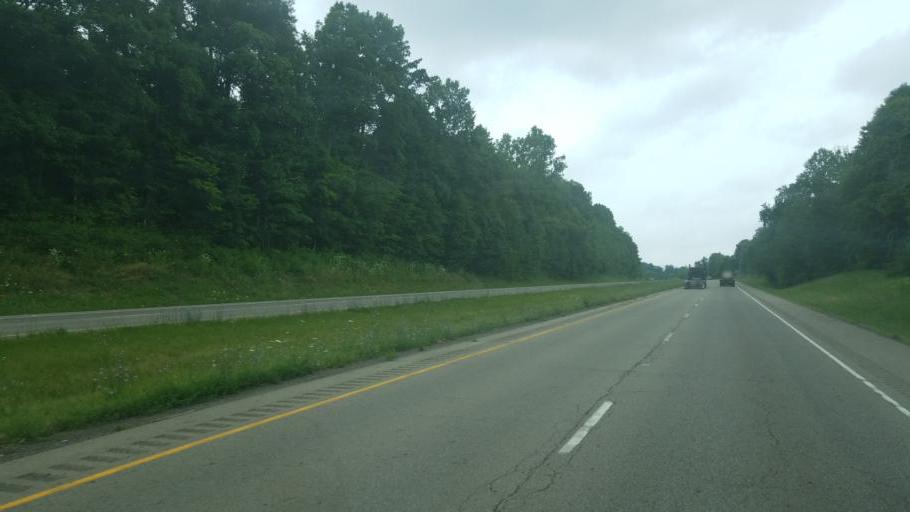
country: US
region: Ohio
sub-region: Richland County
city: Mansfield
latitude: 40.7178
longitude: -82.5027
